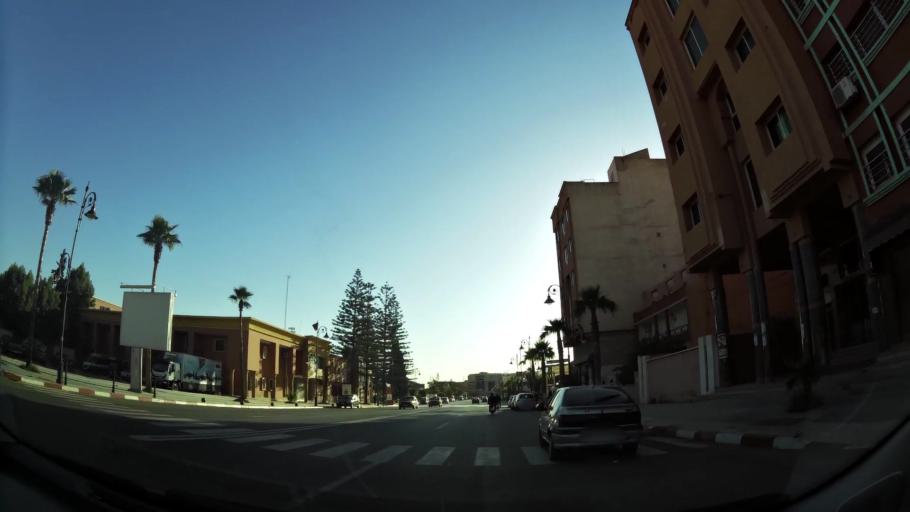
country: MA
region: Oriental
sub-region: Berkane-Taourirt
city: Berkane
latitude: 34.9286
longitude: -2.3251
